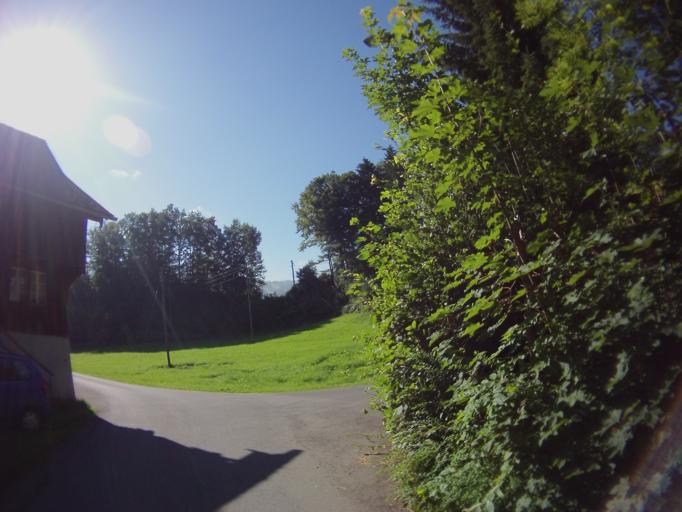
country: CH
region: Schwyz
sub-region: Bezirk Schwyz
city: Sattel
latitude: 47.0881
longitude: 8.6333
